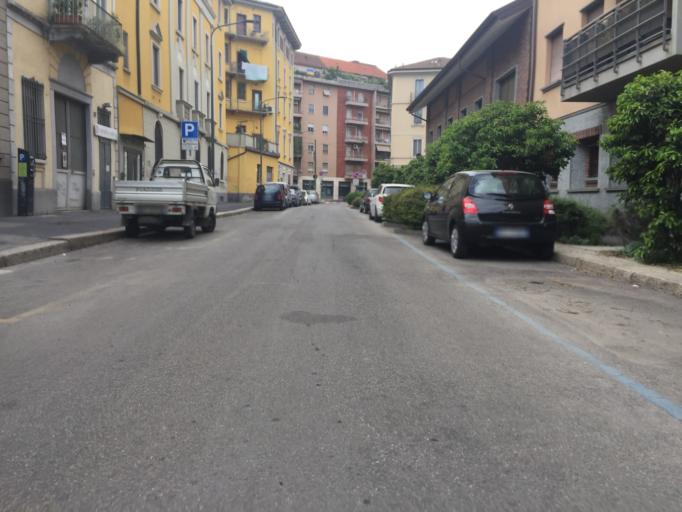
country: IT
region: Lombardy
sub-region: Citta metropolitana di Milano
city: Milano
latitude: 45.4905
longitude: 9.1846
